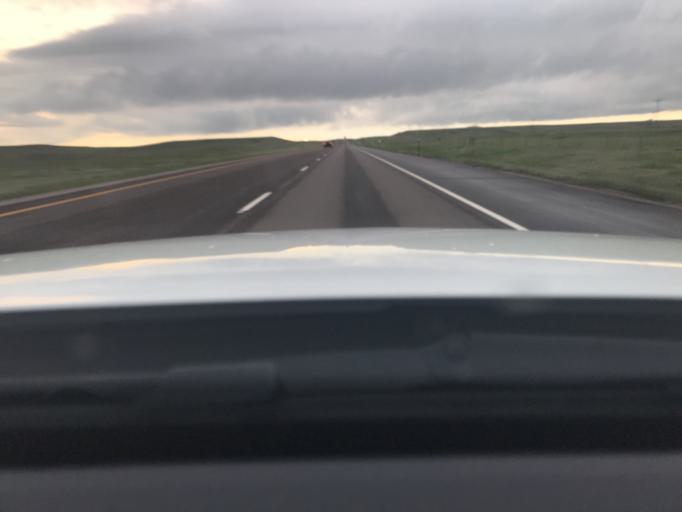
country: US
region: Wyoming
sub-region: Laramie County
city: Ranchettes
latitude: 41.6007
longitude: -104.8652
